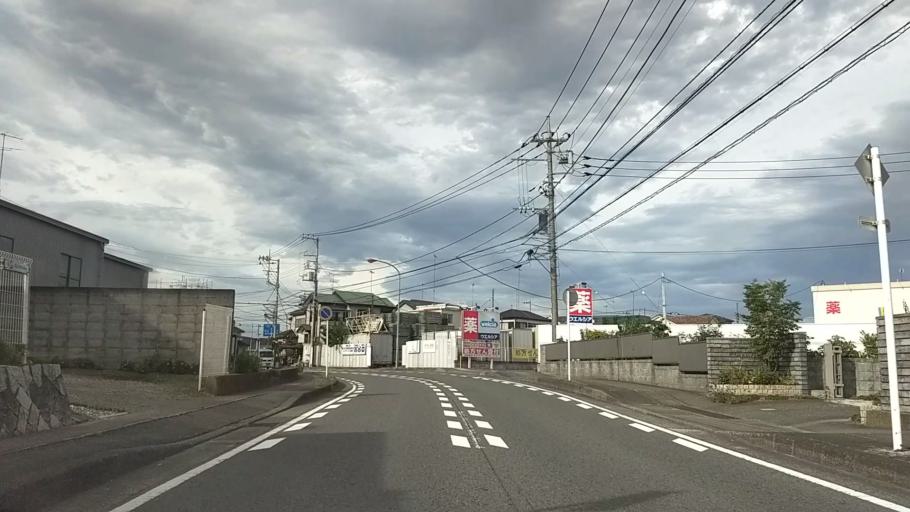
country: JP
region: Kanagawa
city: Zama
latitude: 35.5509
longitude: 139.3327
